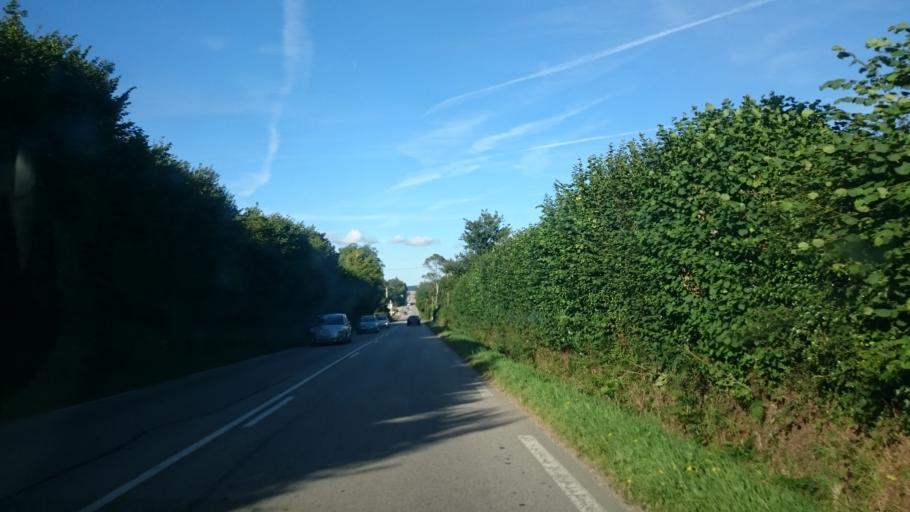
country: FR
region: Lower Normandy
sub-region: Departement de la Manche
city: Martinvast
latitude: 49.5737
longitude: -1.7171
